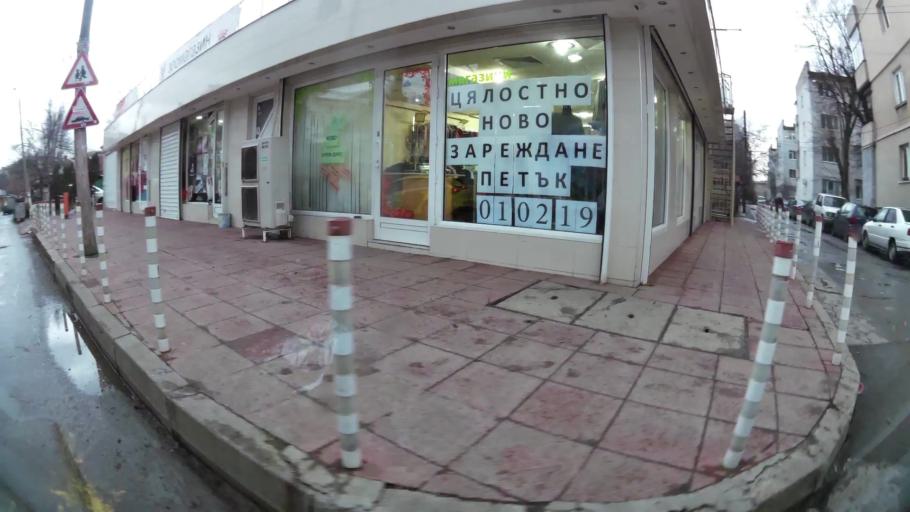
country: BG
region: Sofia-Capital
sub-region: Stolichna Obshtina
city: Sofia
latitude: 42.7348
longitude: 23.3042
